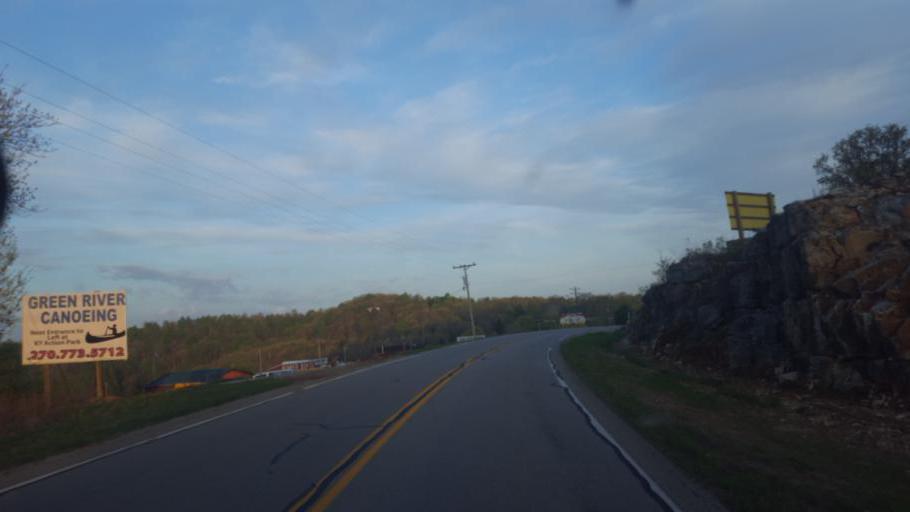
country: US
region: Kentucky
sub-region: Barren County
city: Cave City
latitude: 37.1330
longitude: -86.0029
